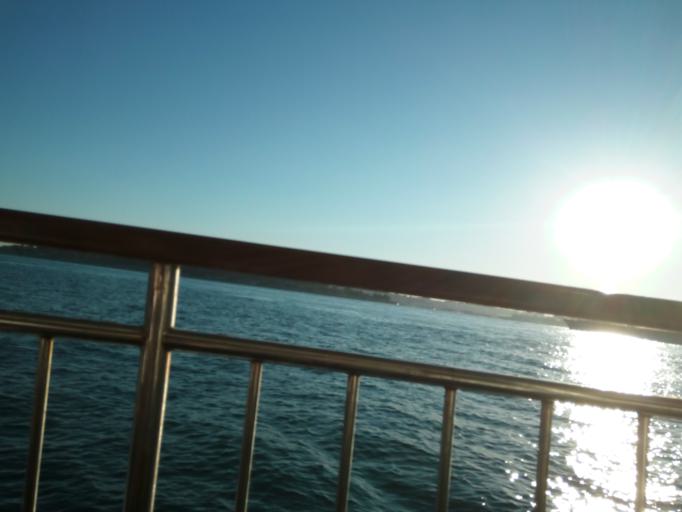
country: TR
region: Istanbul
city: UEskuedar
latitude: 41.0176
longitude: 29.0025
